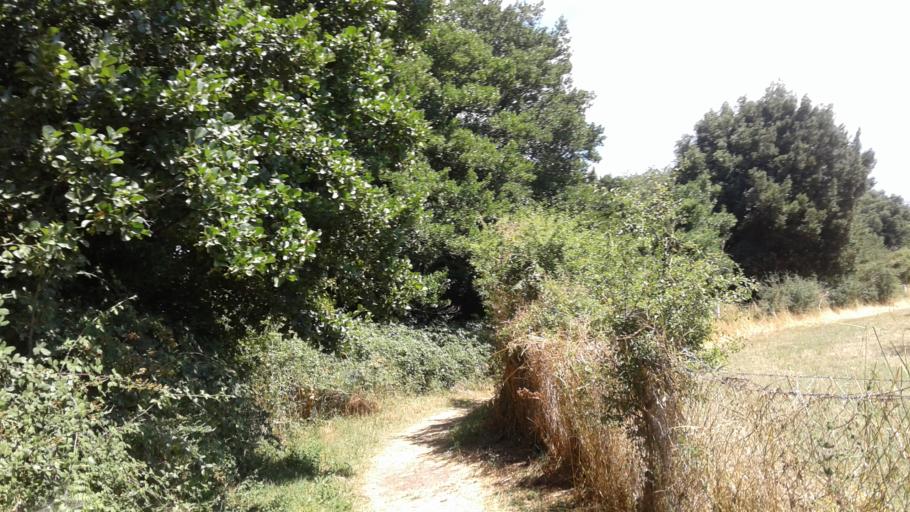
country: IT
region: Sardinia
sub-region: Provincia di Olbia-Tempio
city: Calangianus
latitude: 40.9098
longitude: 9.1709
